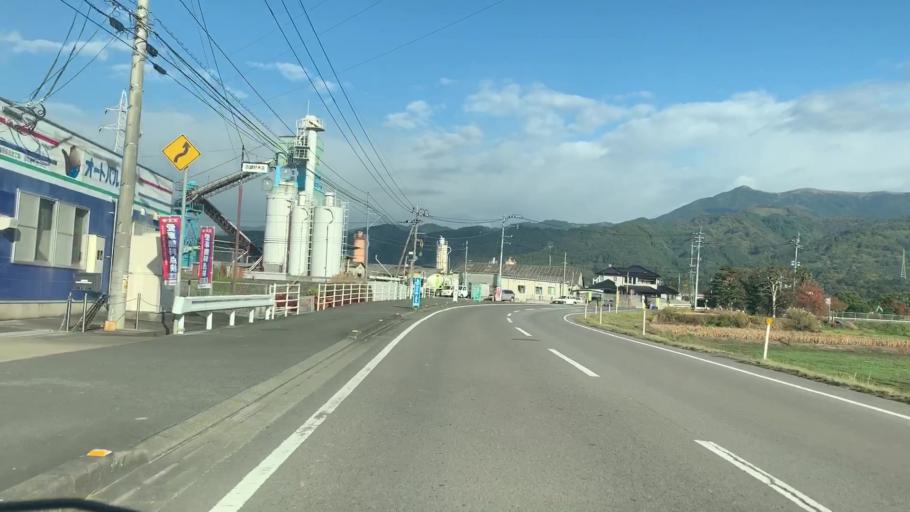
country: JP
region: Saga Prefecture
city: Takeocho-takeo
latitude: 33.2779
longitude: 130.1448
